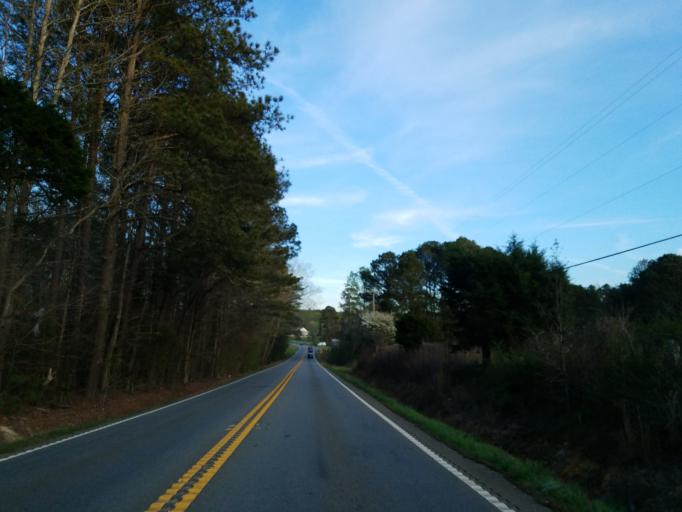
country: US
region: Georgia
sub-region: Cherokee County
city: Holly Springs
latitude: 34.1802
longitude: -84.4327
